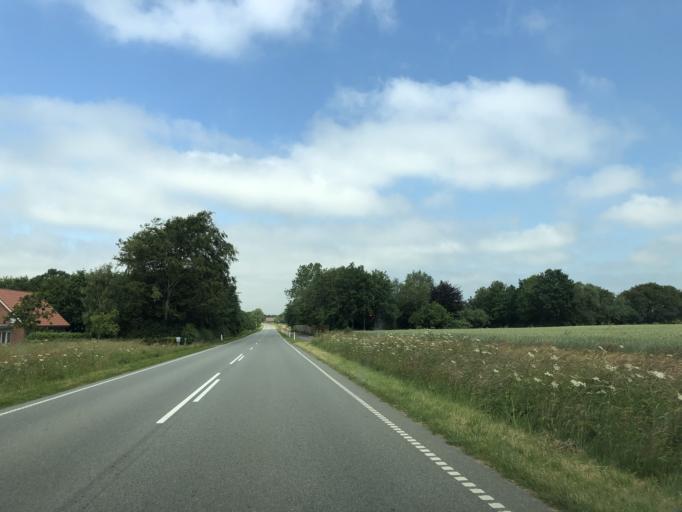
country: DK
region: South Denmark
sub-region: Varde Kommune
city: Varde
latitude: 55.6520
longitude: 8.4886
